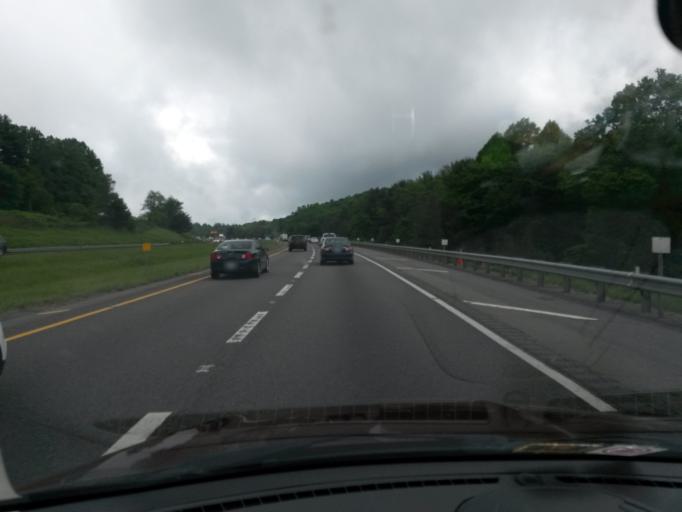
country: US
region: Virginia
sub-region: Carroll County
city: Cana
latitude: 36.6629
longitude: -80.7094
